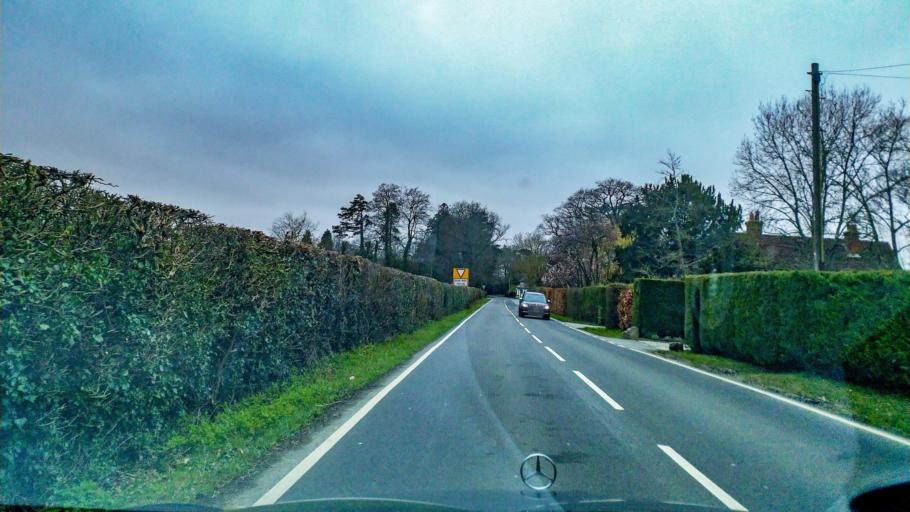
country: GB
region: England
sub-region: West Sussex
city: Langley Green
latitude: 51.1782
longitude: -0.2244
